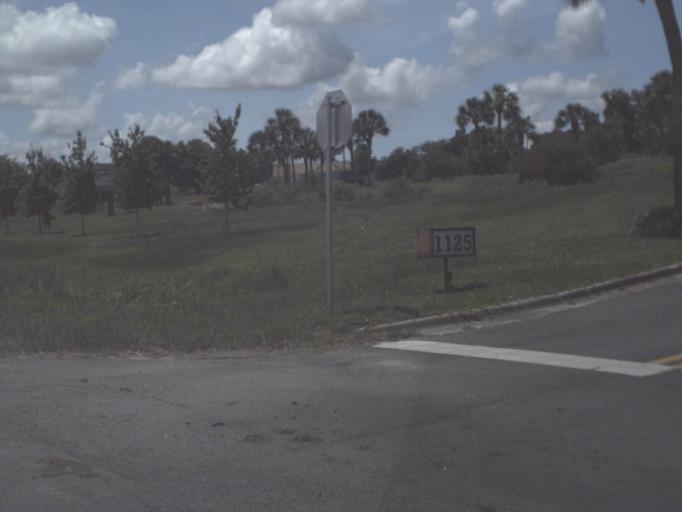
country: US
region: Florida
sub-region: Putnam County
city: Crescent City
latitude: 29.4498
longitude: -81.5123
